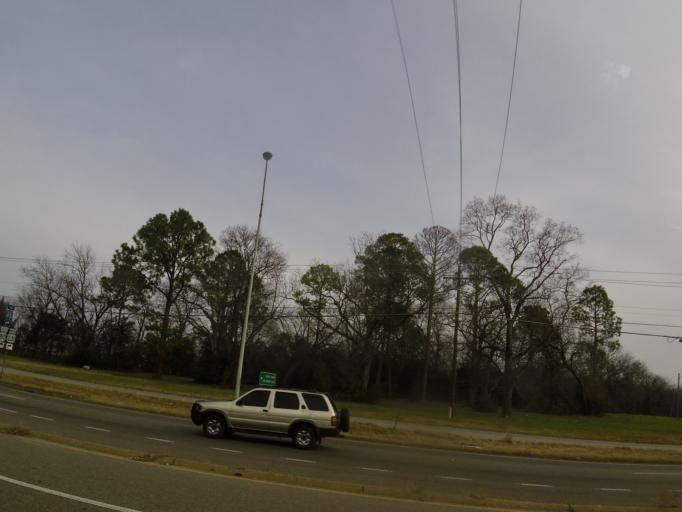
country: US
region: Alabama
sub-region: Montgomery County
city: Montgomery
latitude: 32.3240
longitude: -86.2389
